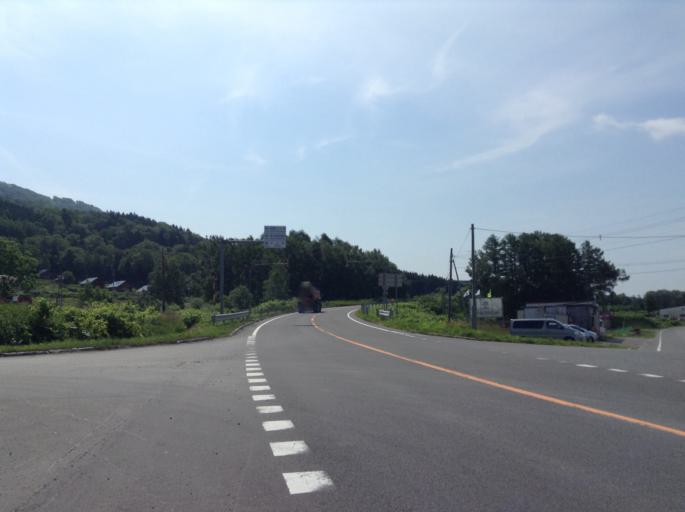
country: JP
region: Hokkaido
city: Nayoro
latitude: 44.7231
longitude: 142.2687
